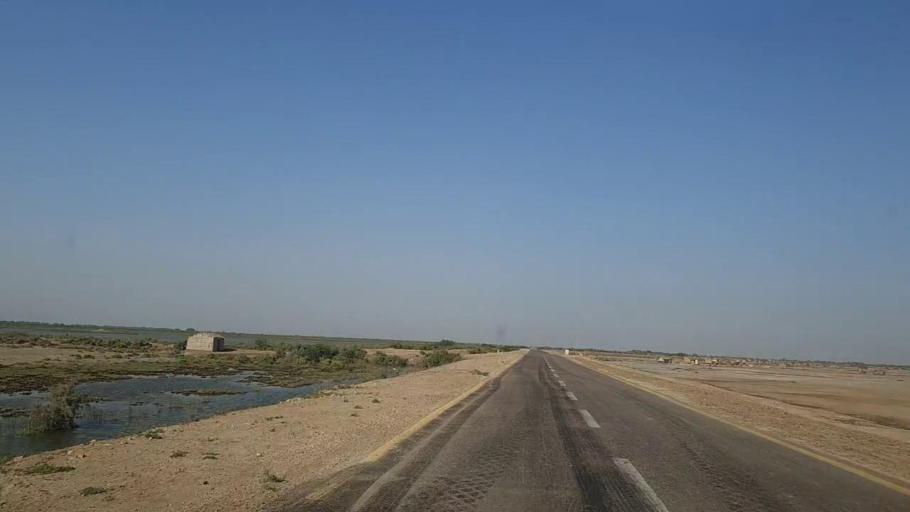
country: PK
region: Sindh
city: Jati
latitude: 24.4370
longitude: 68.3171
